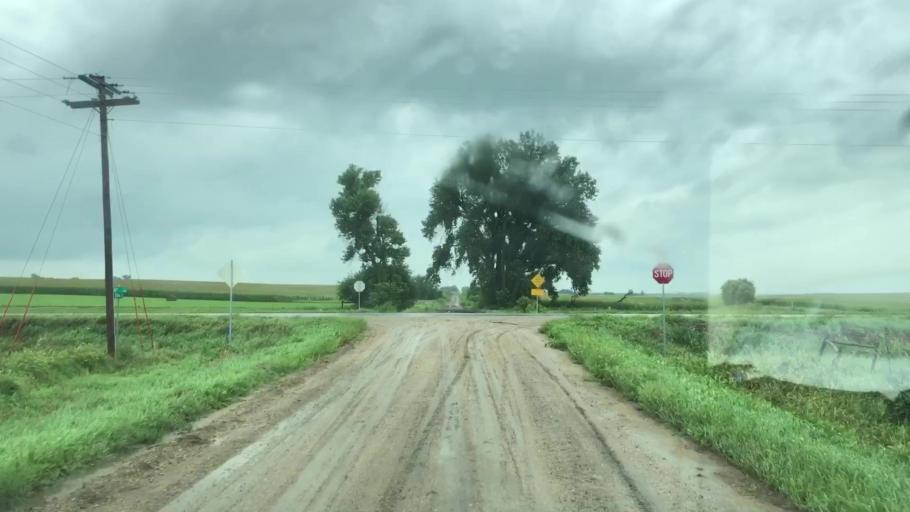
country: US
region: Iowa
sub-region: O'Brien County
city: Sanborn
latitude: 43.2732
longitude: -95.6840
